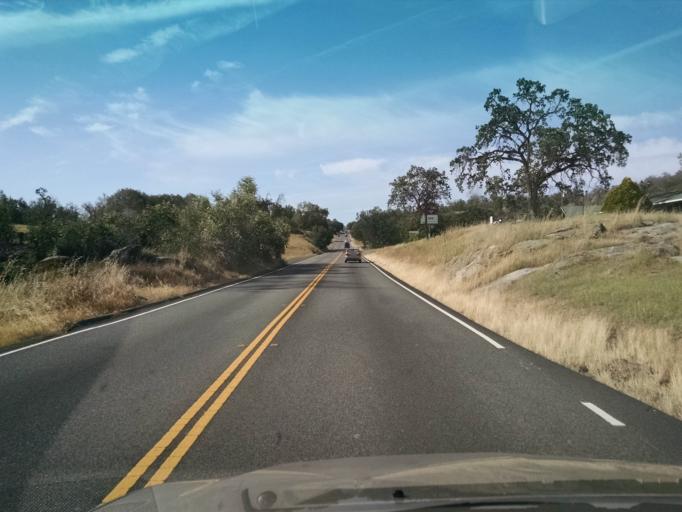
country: US
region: California
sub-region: Madera County
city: Yosemite Lakes
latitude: 37.1512
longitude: -119.7316
